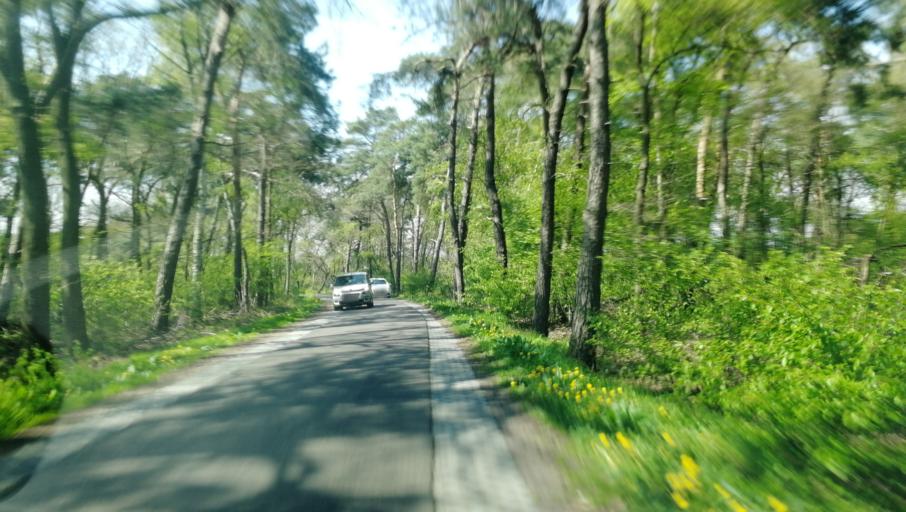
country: NL
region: Limburg
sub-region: Gemeente Peel en Maas
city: Maasbree
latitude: 51.3689
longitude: 5.9835
